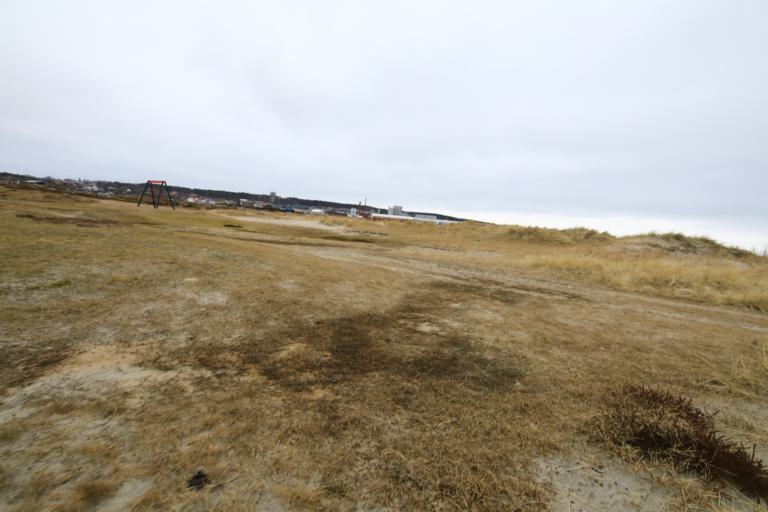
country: SE
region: Halland
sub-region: Kungsbacka Kommun
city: Frillesas
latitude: 57.2447
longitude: 12.1206
